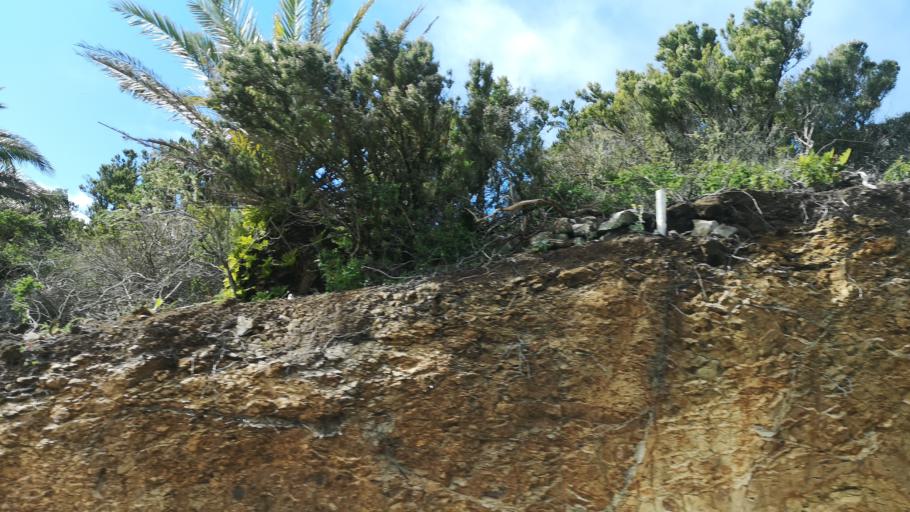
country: ES
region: Canary Islands
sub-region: Provincia de Santa Cruz de Tenerife
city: Vallehermosa
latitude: 28.1446
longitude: -17.3094
